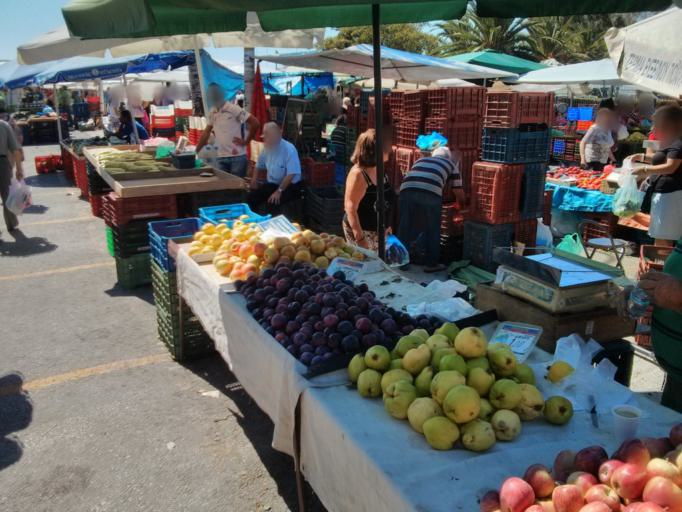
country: GR
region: East Macedonia and Thrace
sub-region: Nomos Kavalas
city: Kavala
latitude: 40.9356
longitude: 24.4043
